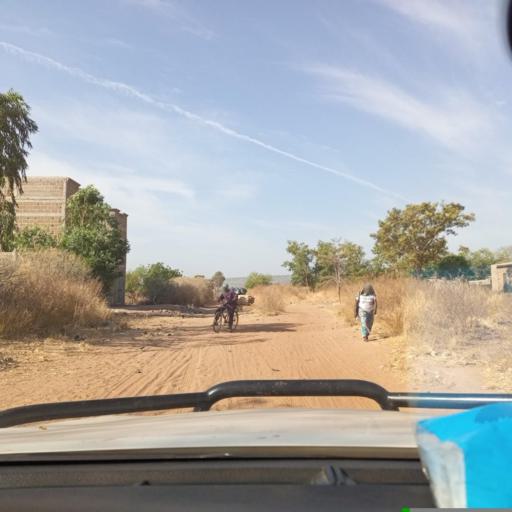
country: ML
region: Bamako
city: Bamako
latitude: 12.5580
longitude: -8.1350
